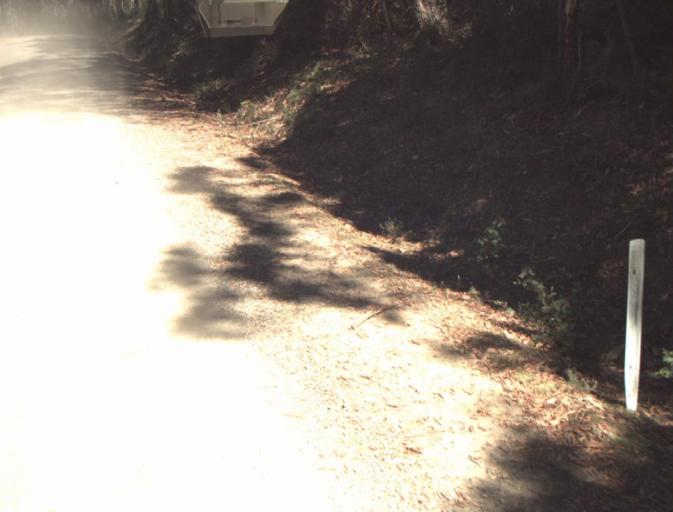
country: AU
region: Tasmania
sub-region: Dorset
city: Scottsdale
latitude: -41.3832
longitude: 147.4964
